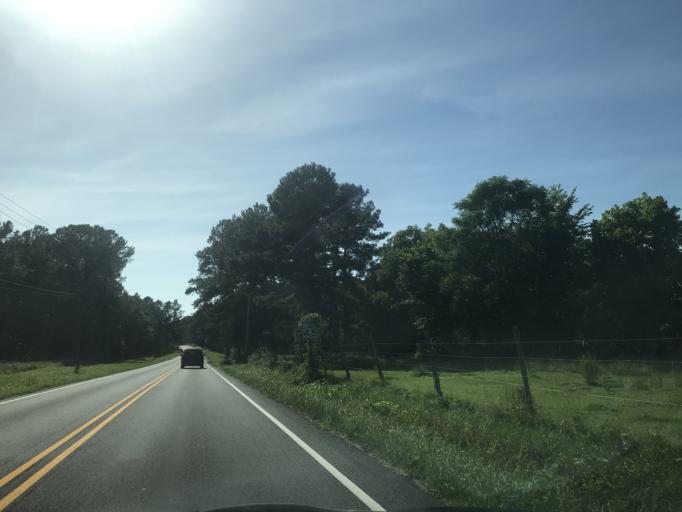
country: US
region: North Carolina
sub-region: Wake County
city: Garner
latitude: 35.6650
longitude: -78.5609
